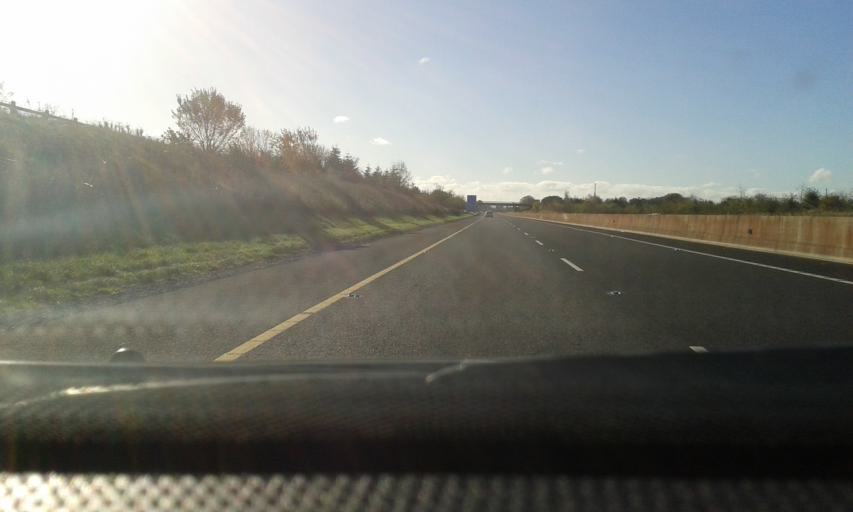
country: IE
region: Munster
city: Thurles
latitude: 52.6373
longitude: -7.7601
